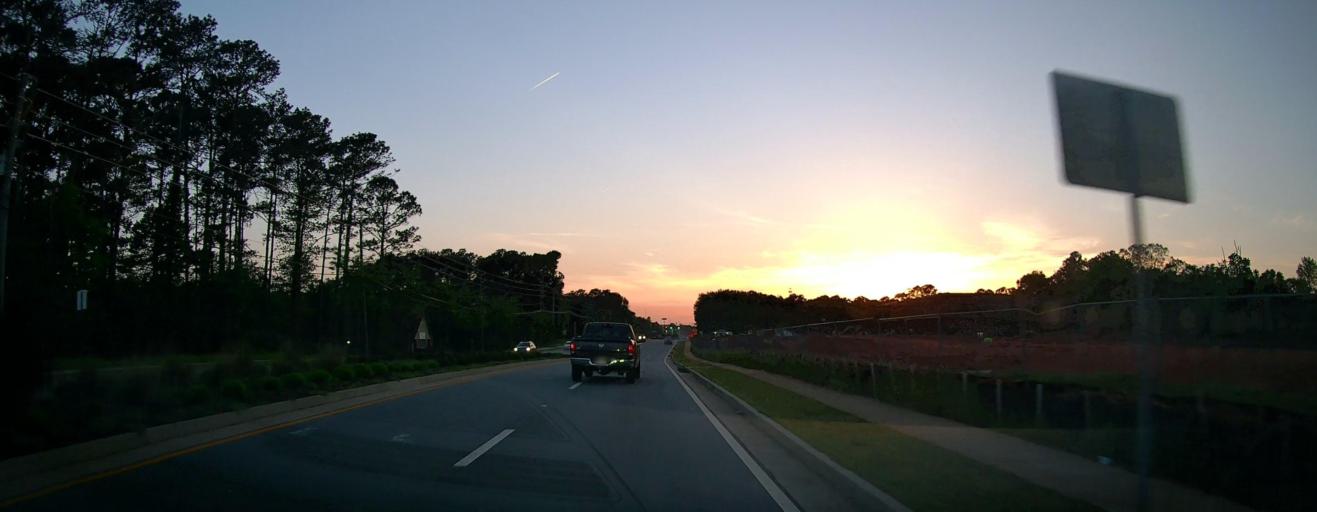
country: US
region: Georgia
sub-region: Henry County
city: McDonough
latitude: 33.4828
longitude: -84.2024
